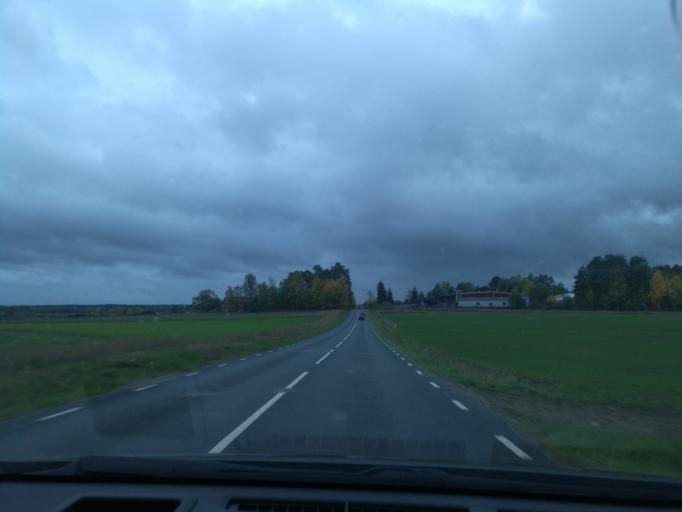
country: SE
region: Soedermanland
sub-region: Vingakers Kommun
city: Vingaker
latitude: 59.0670
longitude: 15.8890
